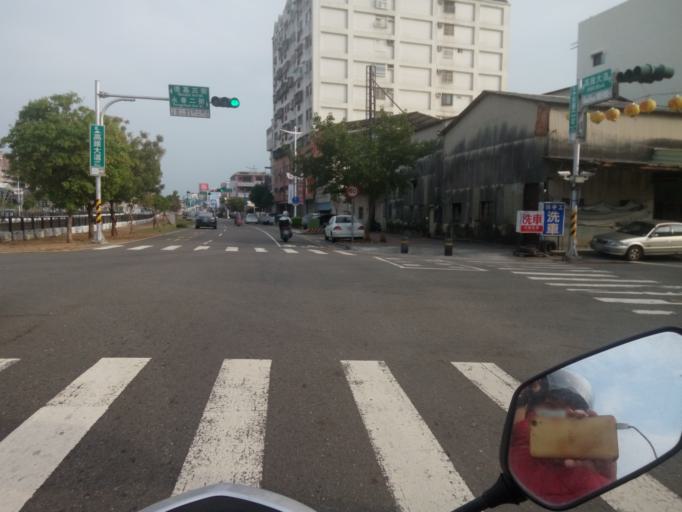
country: TW
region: Taiwan
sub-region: Chiayi
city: Jiayi Shi
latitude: 23.4788
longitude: 120.4261
